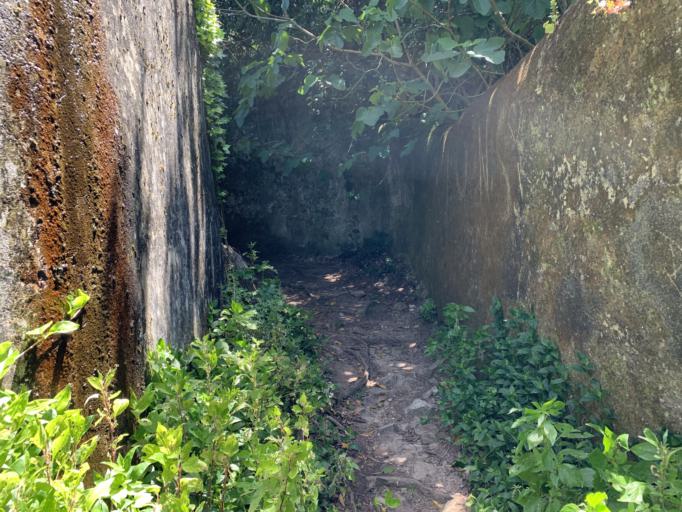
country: PT
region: Lisbon
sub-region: Sintra
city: Sintra
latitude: 38.7945
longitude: -9.3989
